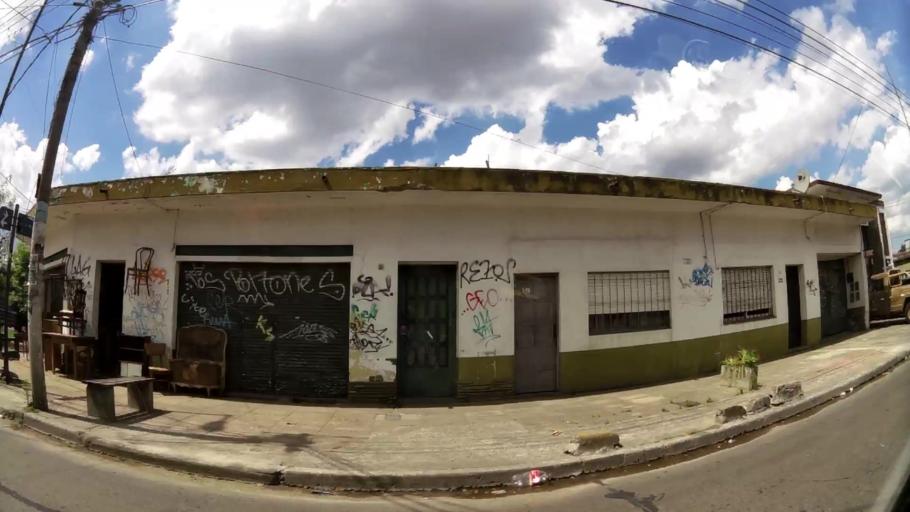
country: AR
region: Buenos Aires
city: Ituzaingo
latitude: -34.6465
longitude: -58.6669
